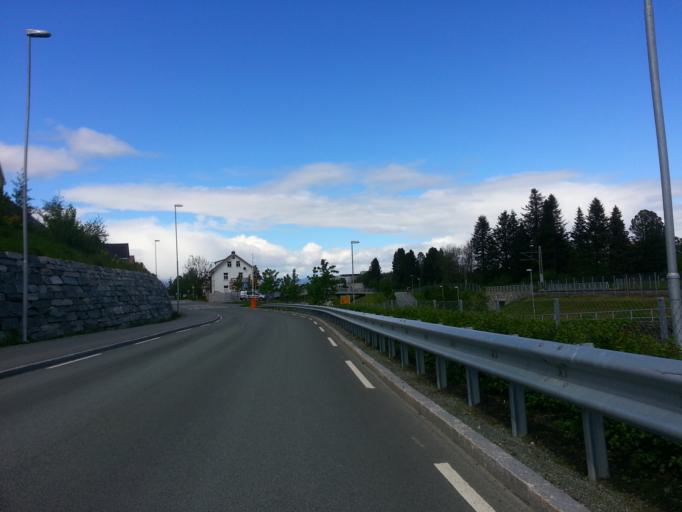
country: NO
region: Sor-Trondelag
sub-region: Trondheim
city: Trondheim
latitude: 63.4114
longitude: 10.3829
